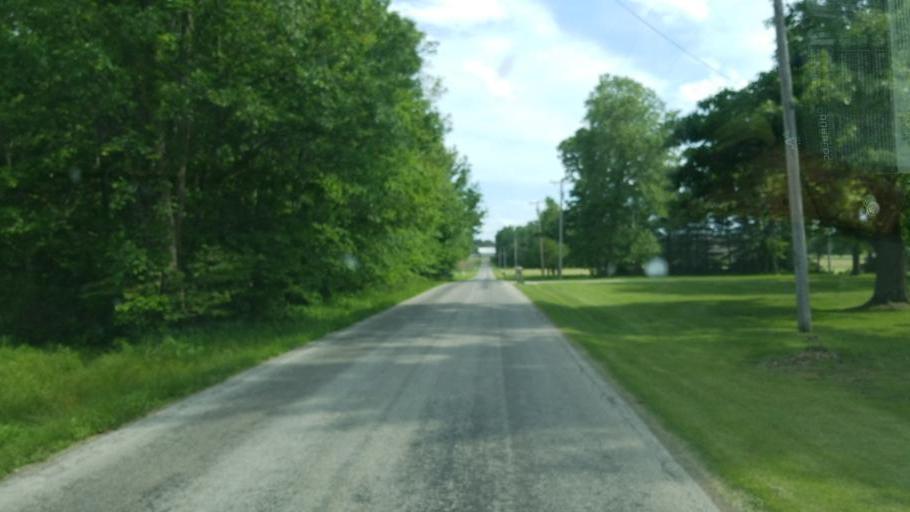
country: US
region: Ohio
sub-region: Richland County
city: Lincoln Heights
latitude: 40.8737
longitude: -82.5328
